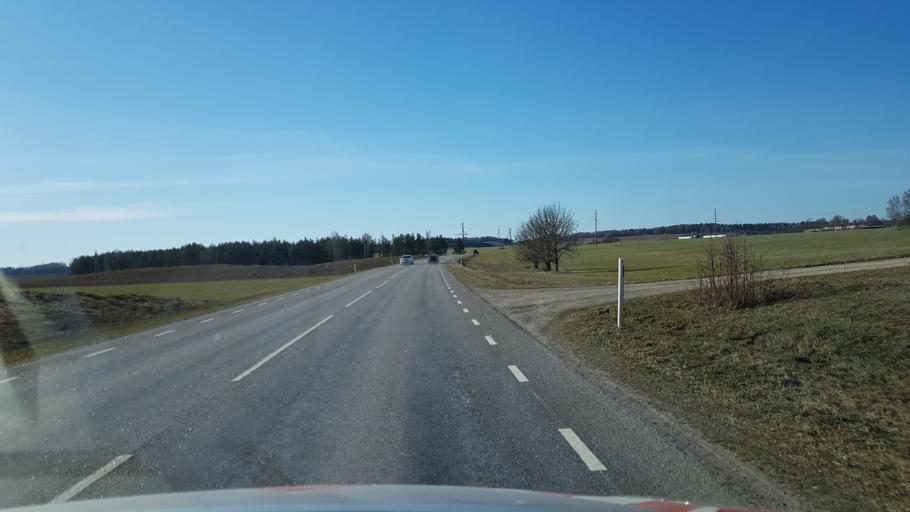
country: EE
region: Laeaene-Virumaa
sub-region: Vinni vald
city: Vinni
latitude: 59.3154
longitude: 26.4456
